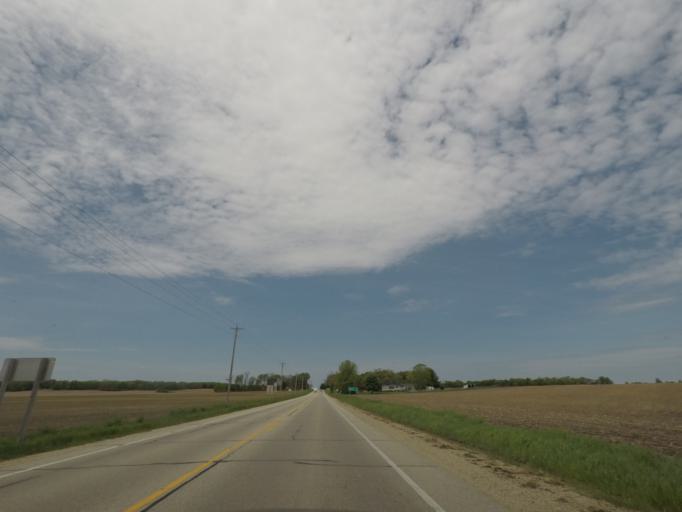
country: US
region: Wisconsin
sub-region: Rock County
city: Evansville
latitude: 42.8267
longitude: -89.3048
